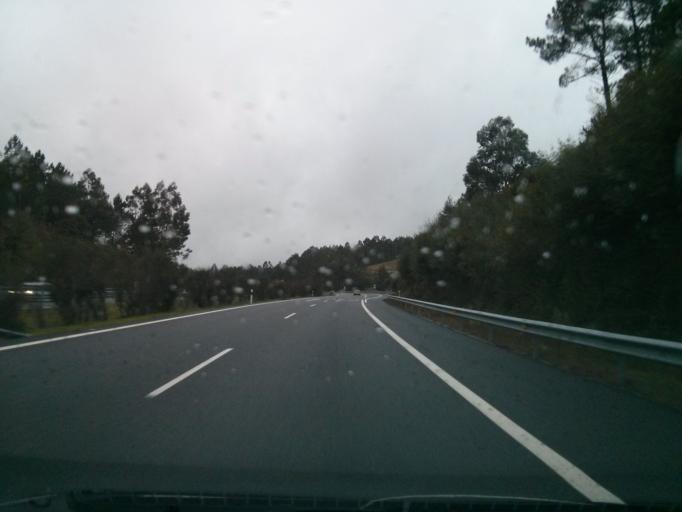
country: ES
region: Galicia
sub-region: Provincia de Ourense
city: Melon
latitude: 42.2185
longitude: -8.2535
